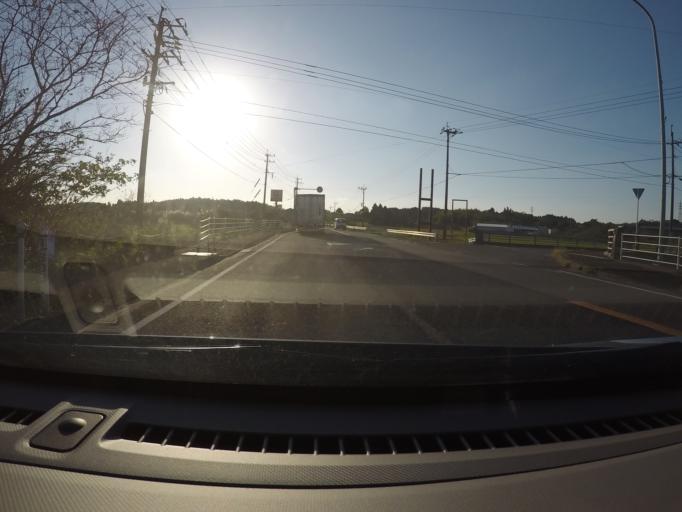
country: JP
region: Kagoshima
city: Akune
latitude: 32.0801
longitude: 130.2665
